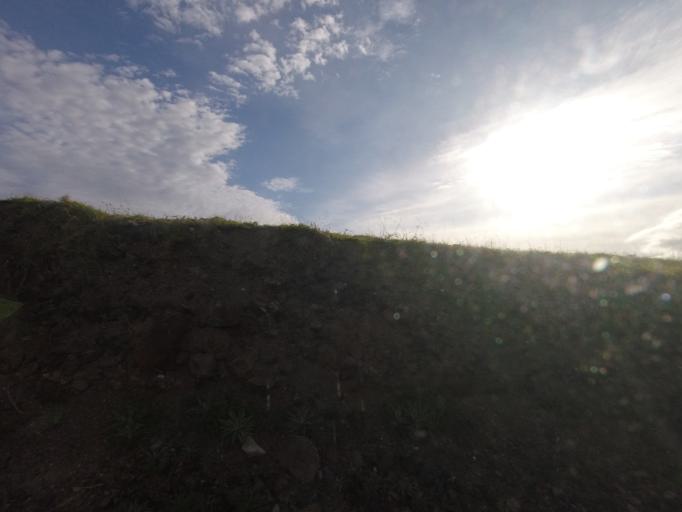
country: PT
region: Madeira
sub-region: Machico
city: Canical
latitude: 32.7477
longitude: -16.7402
